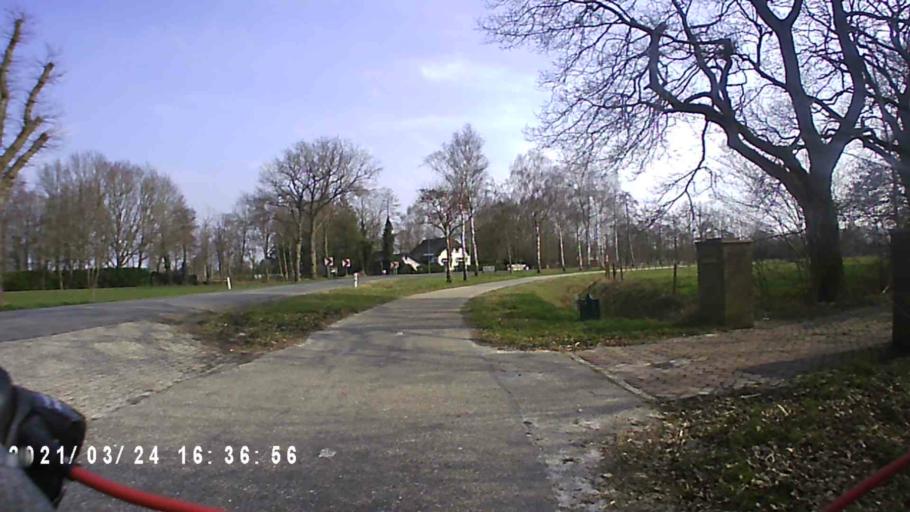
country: NL
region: Groningen
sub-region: Gemeente Leek
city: Leek
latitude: 53.0632
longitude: 6.2814
